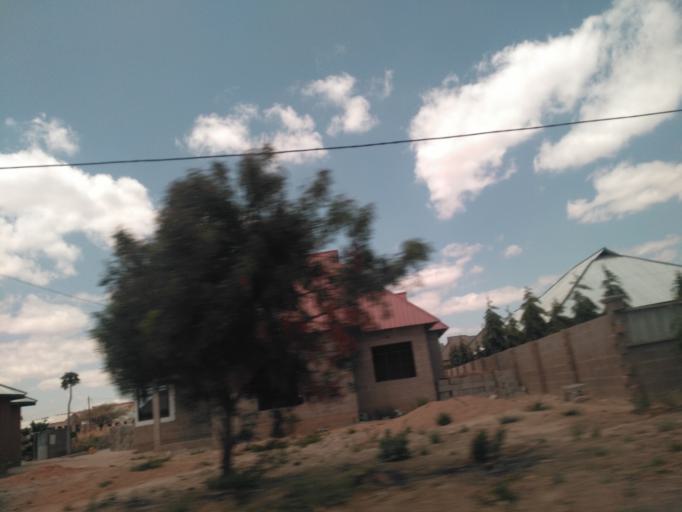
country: TZ
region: Dodoma
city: Kisasa
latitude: -6.1807
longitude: 35.7955
